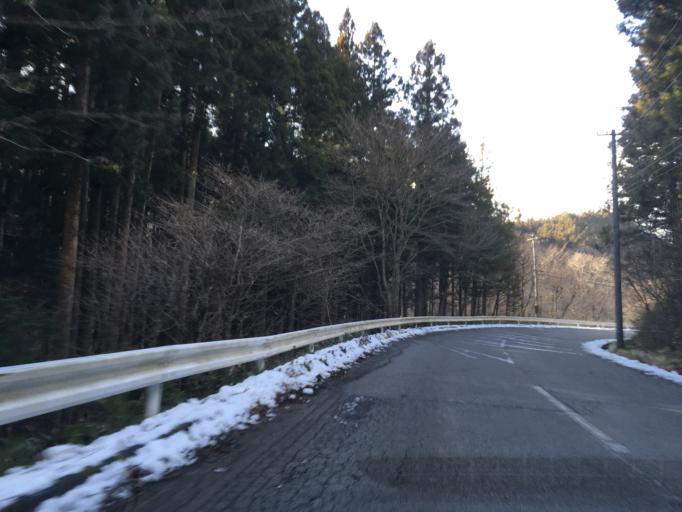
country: JP
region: Miyagi
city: Furukawa
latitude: 38.8041
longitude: 140.8292
